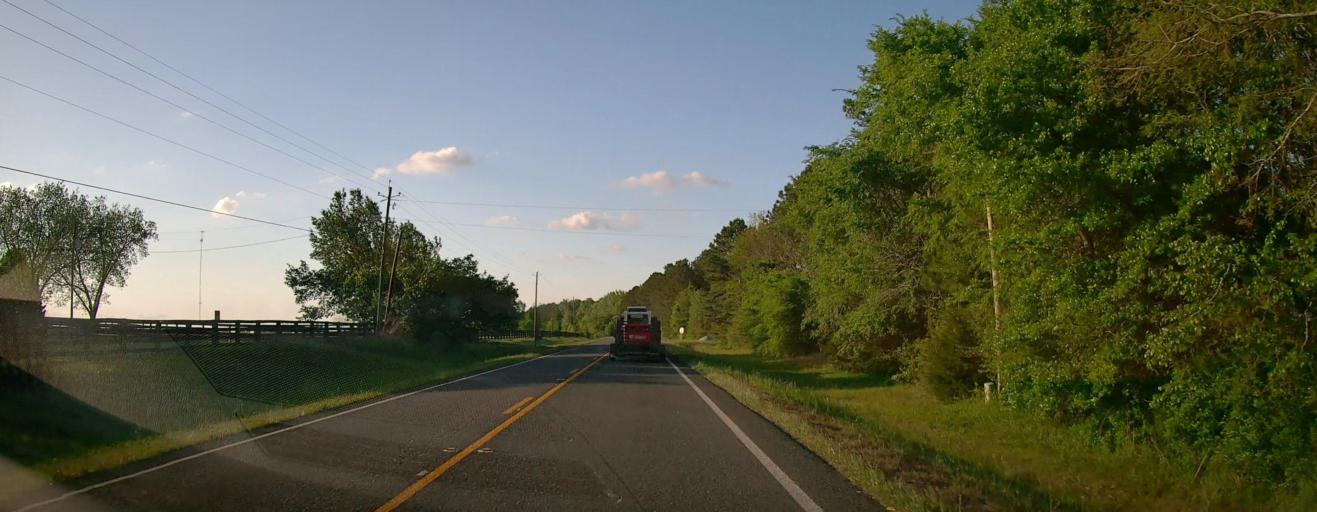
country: US
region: Georgia
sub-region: Jasper County
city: Monticello
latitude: 33.4362
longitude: -83.6198
